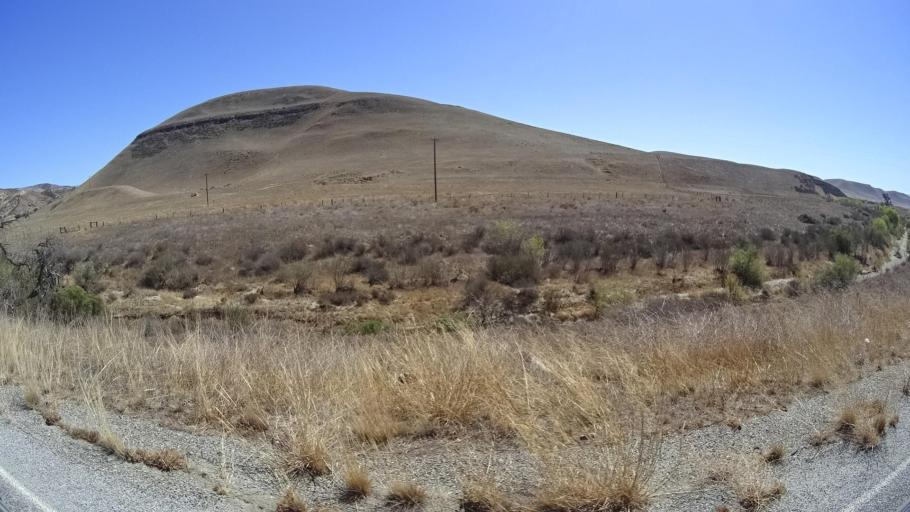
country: US
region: California
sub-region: Monterey County
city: King City
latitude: 36.2644
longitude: -121.0809
